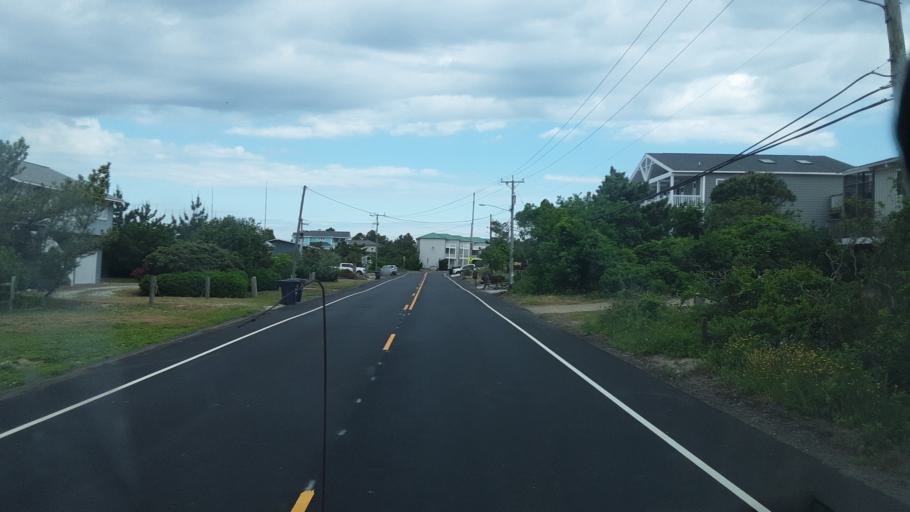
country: US
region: Virginia
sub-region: City of Virginia Beach
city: Virginia Beach
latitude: 36.7154
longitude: -75.9340
